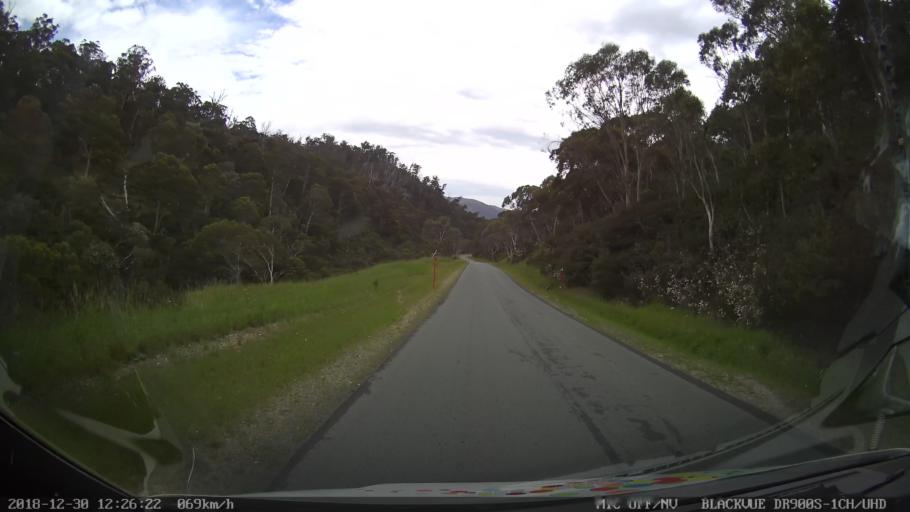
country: AU
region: New South Wales
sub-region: Snowy River
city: Jindabyne
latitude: -36.3400
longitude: 148.4893
